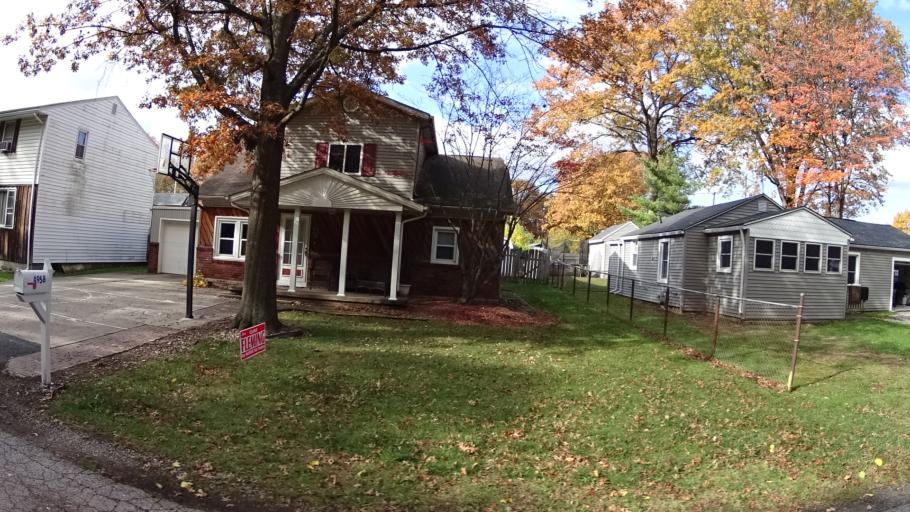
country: US
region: Ohio
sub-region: Lorain County
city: Sheffield
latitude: 41.4237
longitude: -82.1128
